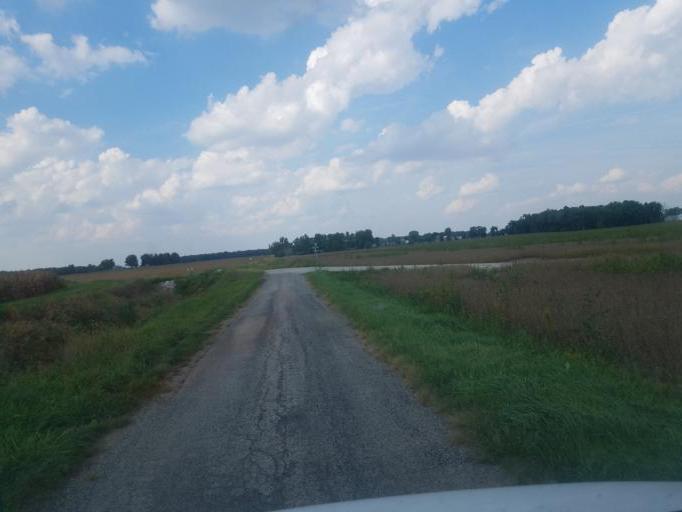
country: US
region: Ohio
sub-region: Hancock County
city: Arlington
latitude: 40.8046
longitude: -83.6897
